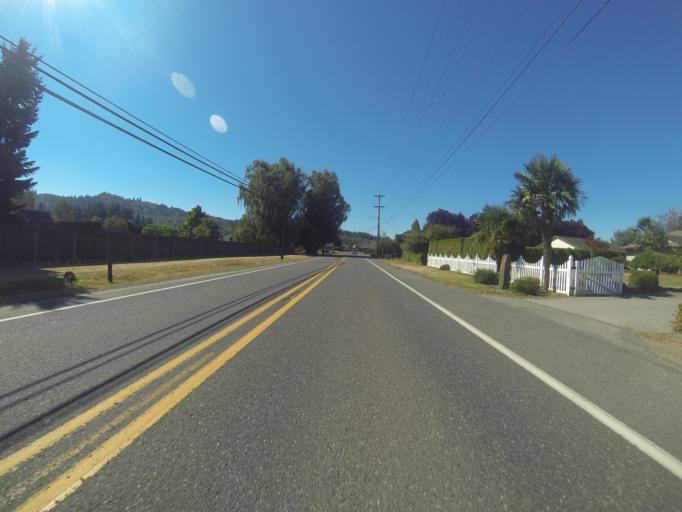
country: US
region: Washington
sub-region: Cowlitz County
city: Woodland
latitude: 45.9217
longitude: -122.7252
